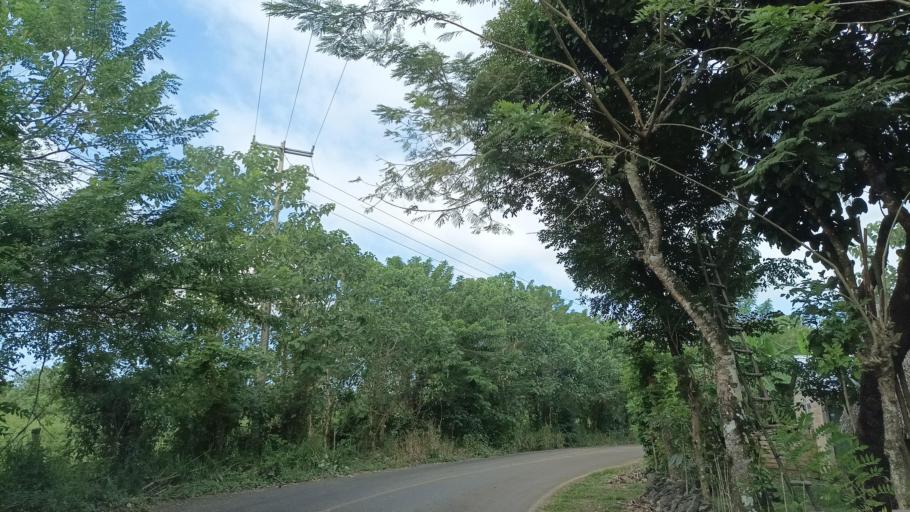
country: MX
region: Veracruz
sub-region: Pajapan
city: Pajapan
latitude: 18.1858
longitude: -94.6752
